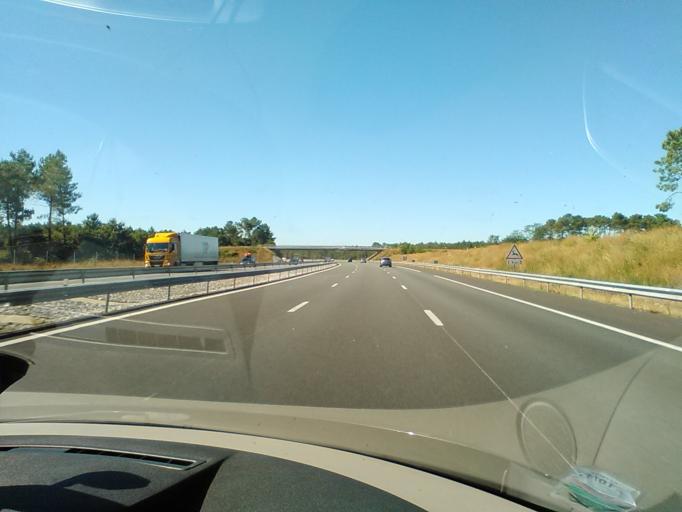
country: FR
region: Aquitaine
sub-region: Departement des Landes
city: Magescq
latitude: 43.7744
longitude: -1.2153
